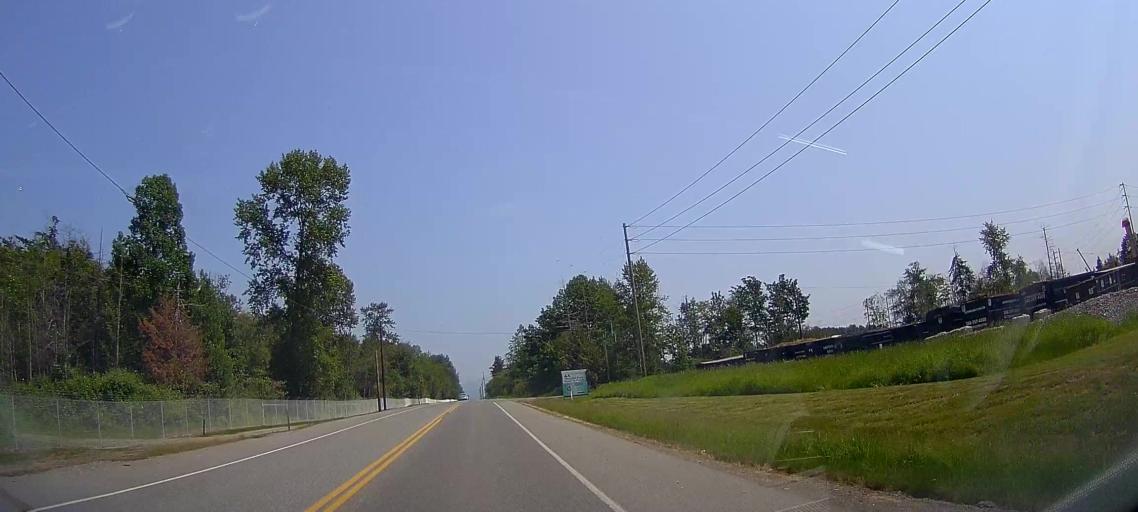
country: US
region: Washington
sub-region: Skagit County
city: Mount Vernon
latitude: 48.4576
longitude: -122.4393
